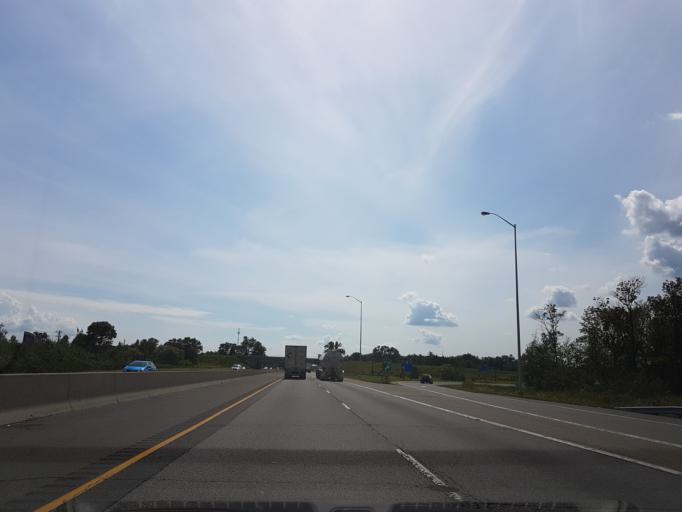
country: CA
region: Ontario
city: Prescott
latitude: 44.7251
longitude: -75.5220
